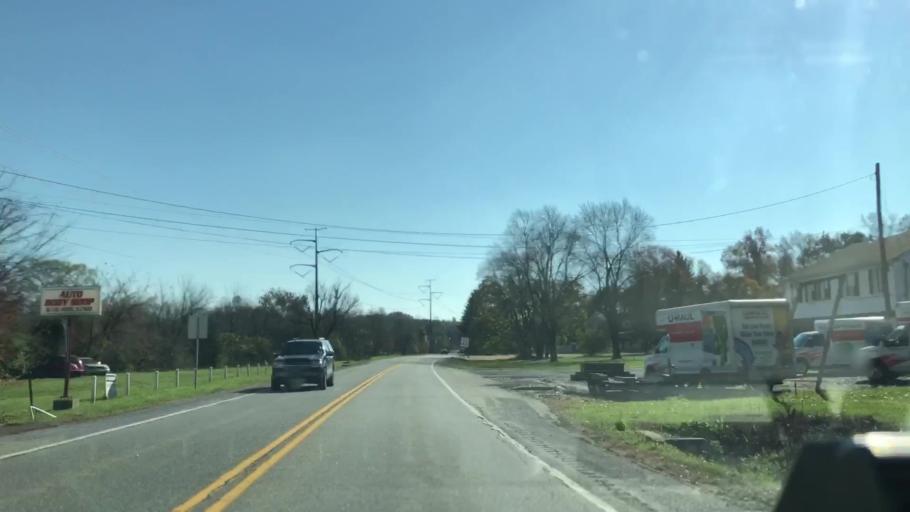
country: US
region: Pennsylvania
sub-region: Montgomery County
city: Sanatoga
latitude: 40.2021
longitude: -75.5860
